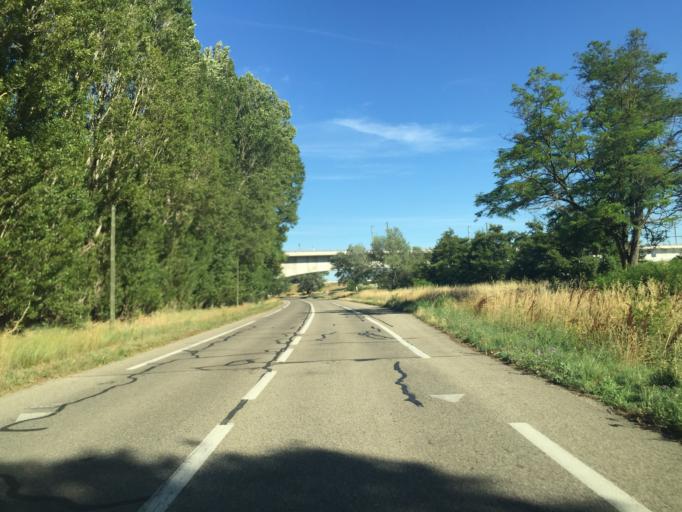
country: FR
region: Languedoc-Roussillon
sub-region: Departement du Gard
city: Montfaucon
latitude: 44.0766
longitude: 4.7649
